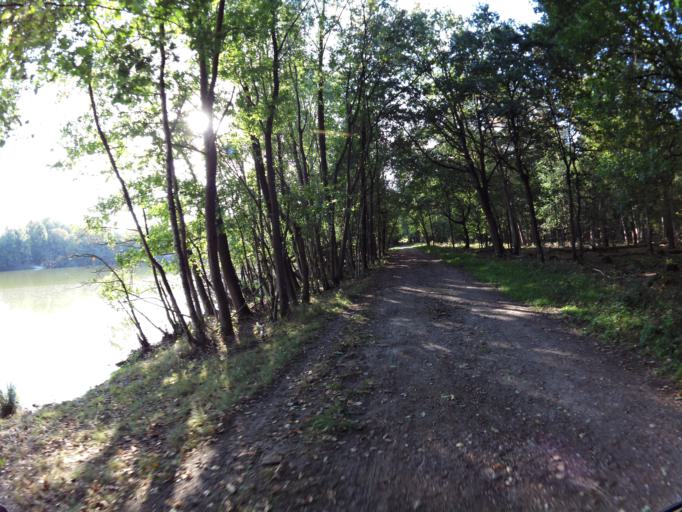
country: DE
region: North Rhine-Westphalia
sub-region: Regierungsbezirk Koln
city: Gangelt
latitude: 50.9770
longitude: 6.0142
